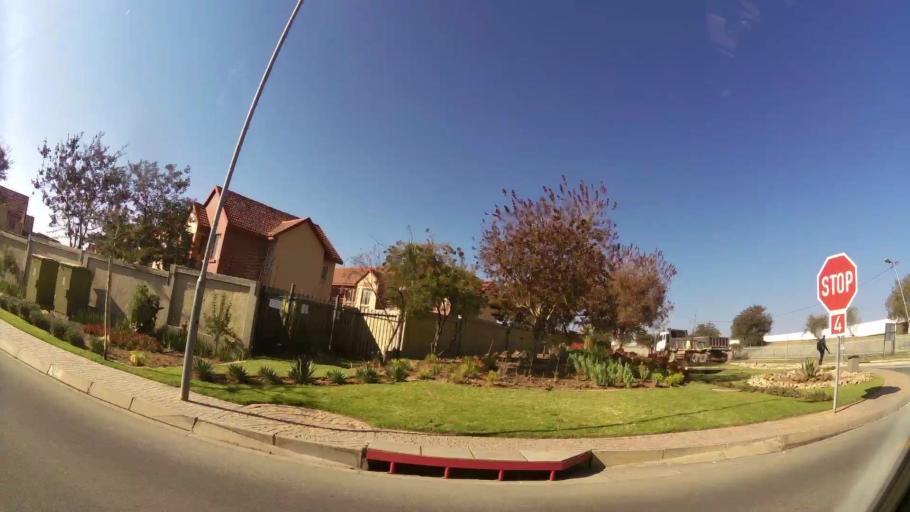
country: ZA
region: Gauteng
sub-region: City of Johannesburg Metropolitan Municipality
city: Midrand
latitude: -25.9180
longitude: 28.1276
